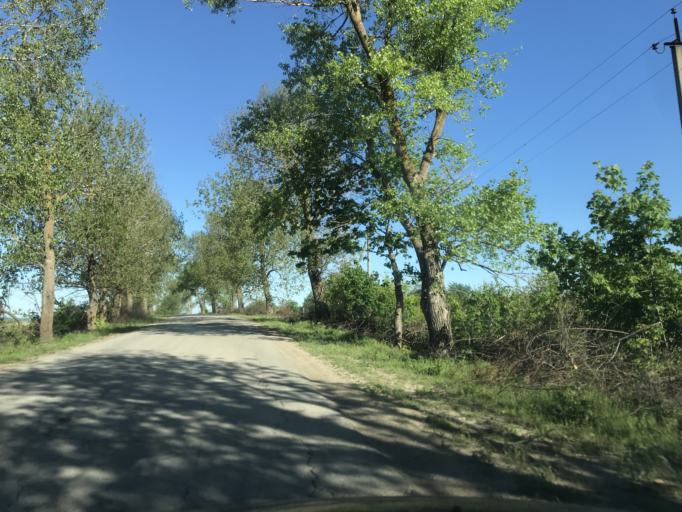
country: MD
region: Orhei
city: Orhei
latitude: 47.2610
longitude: 28.7931
